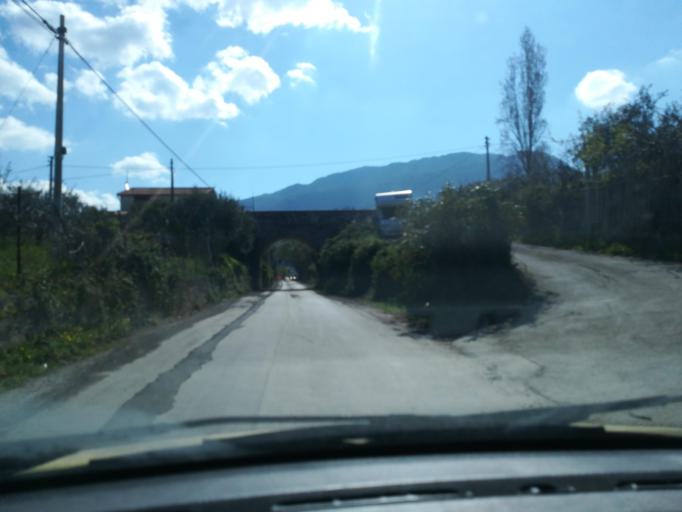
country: IT
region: Sicily
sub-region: Palermo
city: Cannizzaro-Favara
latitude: 38.0468
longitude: 13.2663
